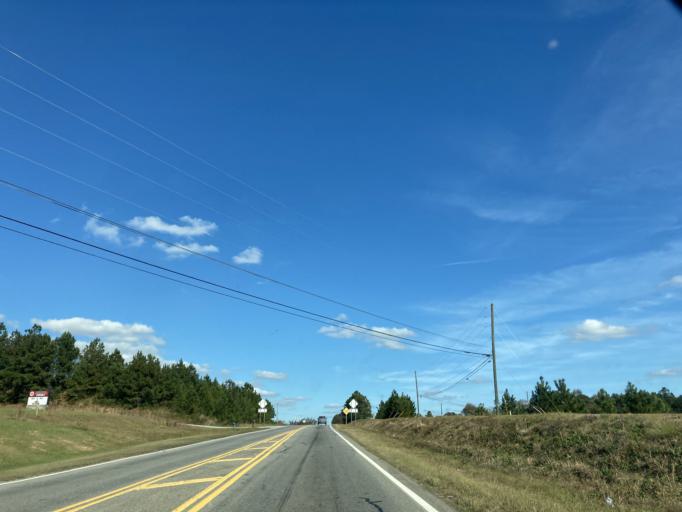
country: US
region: Georgia
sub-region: Bibb County
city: Macon
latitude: 32.8900
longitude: -83.5357
